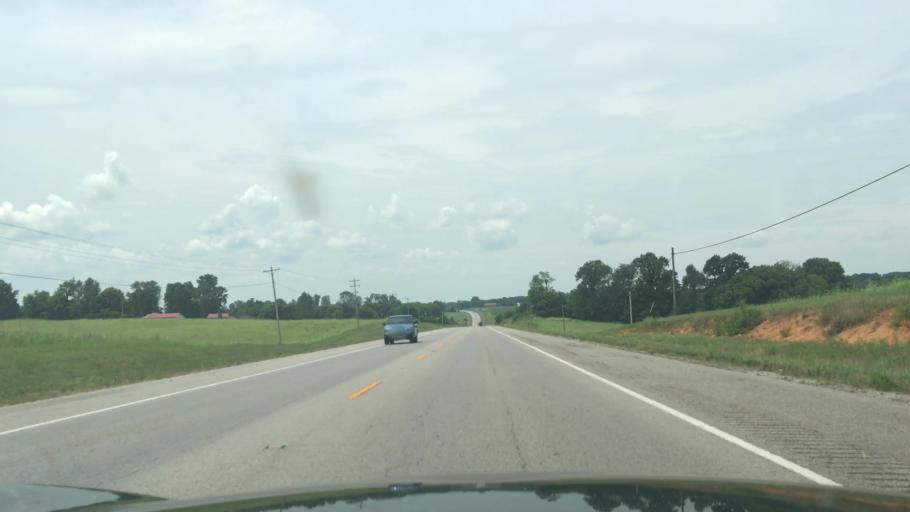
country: US
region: Kentucky
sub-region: Green County
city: Greensburg
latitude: 37.2985
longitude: -85.4552
